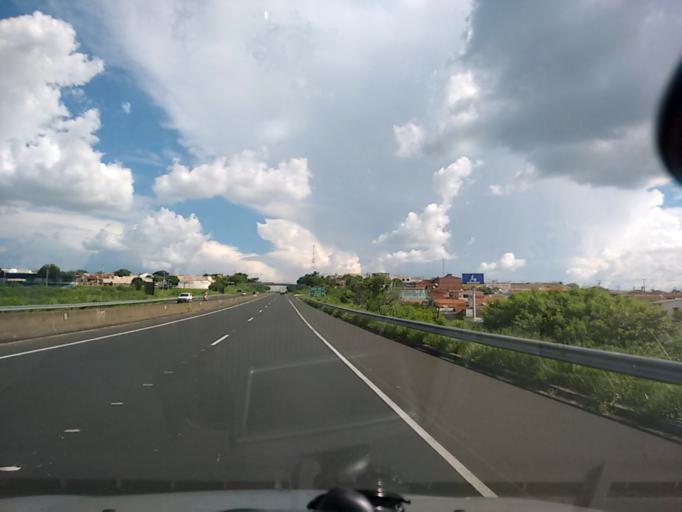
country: BR
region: Sao Paulo
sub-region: Marilia
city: Marilia
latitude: -22.1997
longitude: -49.9649
